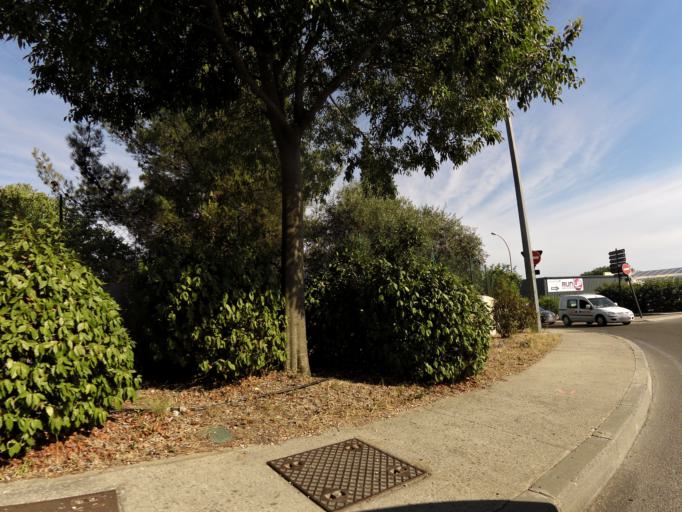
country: FR
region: Languedoc-Roussillon
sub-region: Departement du Gard
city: Milhaud
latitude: 43.8155
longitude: 4.3139
